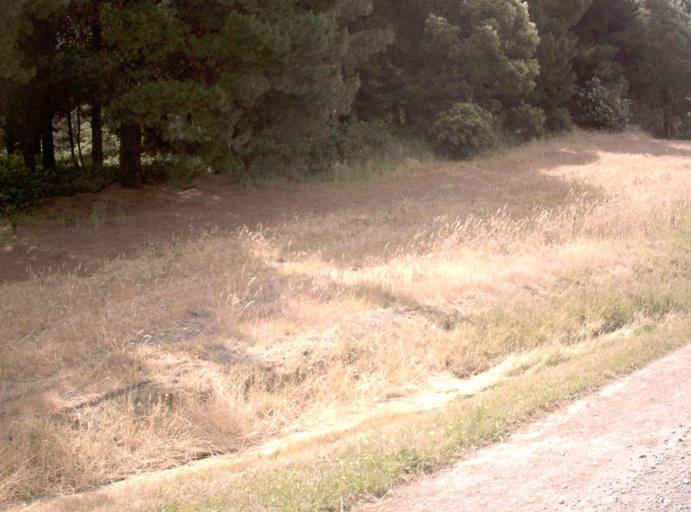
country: AU
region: Victoria
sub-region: Latrobe
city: Traralgon
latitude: -38.3894
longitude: 146.6608
